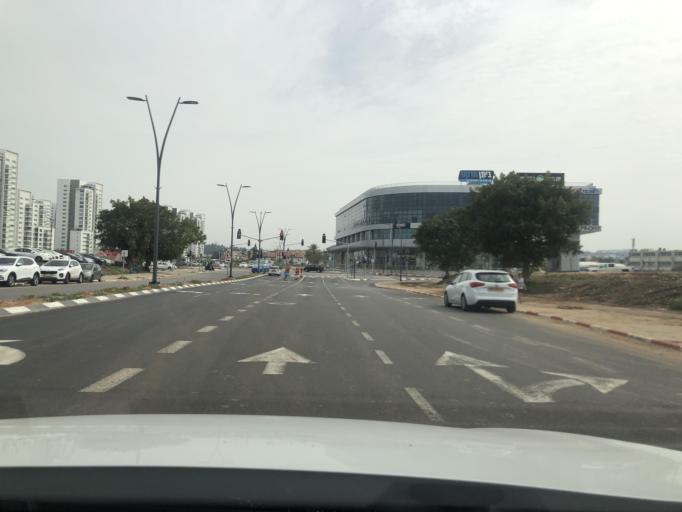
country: IL
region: Central District
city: Rosh Ha'Ayin
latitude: 32.1054
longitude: 34.9407
